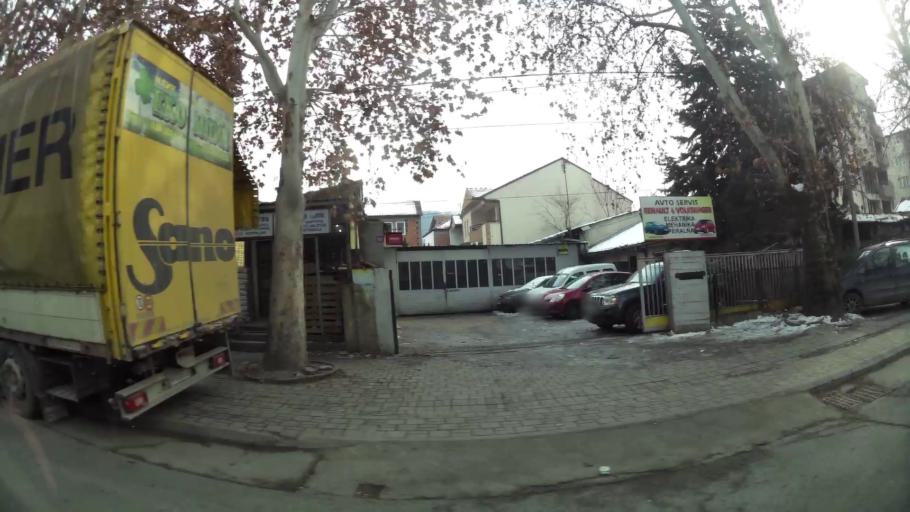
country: MK
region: Cair
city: Cair
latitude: 42.0106
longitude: 21.4444
